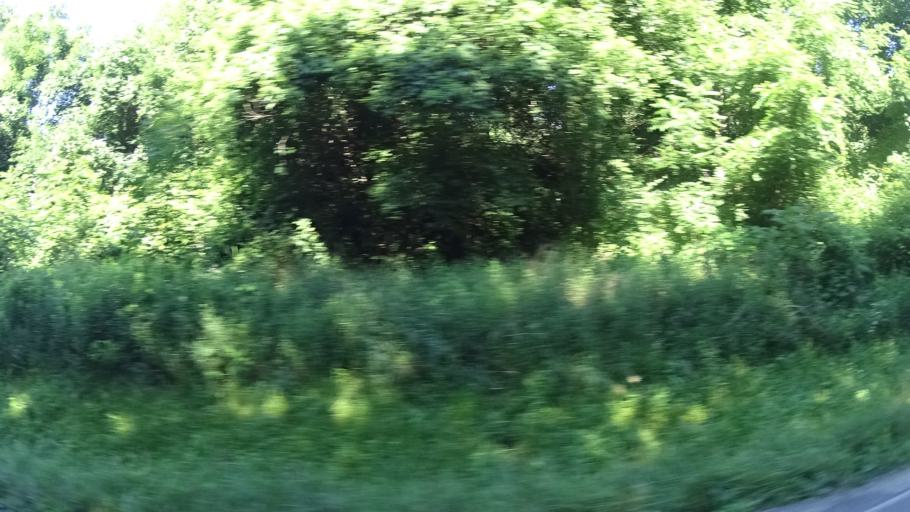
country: US
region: Indiana
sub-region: Madison County
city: Pendleton
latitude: 39.9969
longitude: -85.7563
